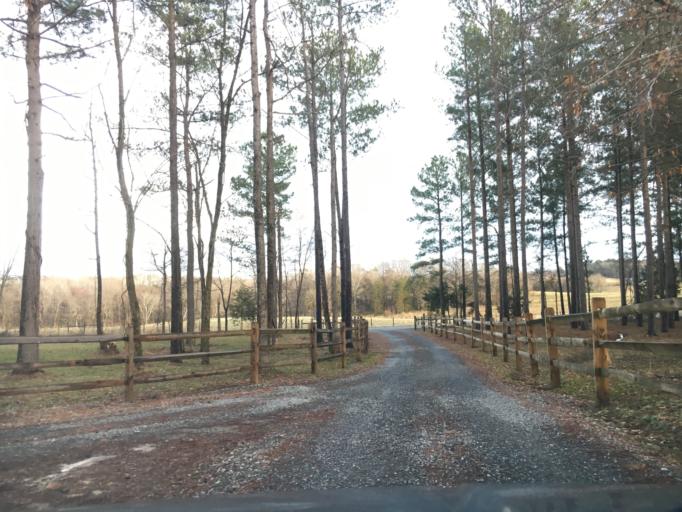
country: US
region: Virginia
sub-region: Halifax County
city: Mountain Road
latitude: 36.6849
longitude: -79.0331
